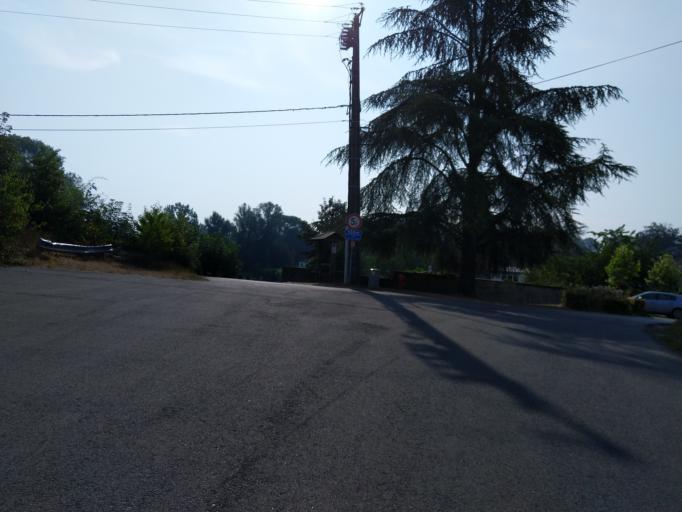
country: BE
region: Wallonia
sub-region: Province du Hainaut
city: Seneffe
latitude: 50.5671
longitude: 4.2568
